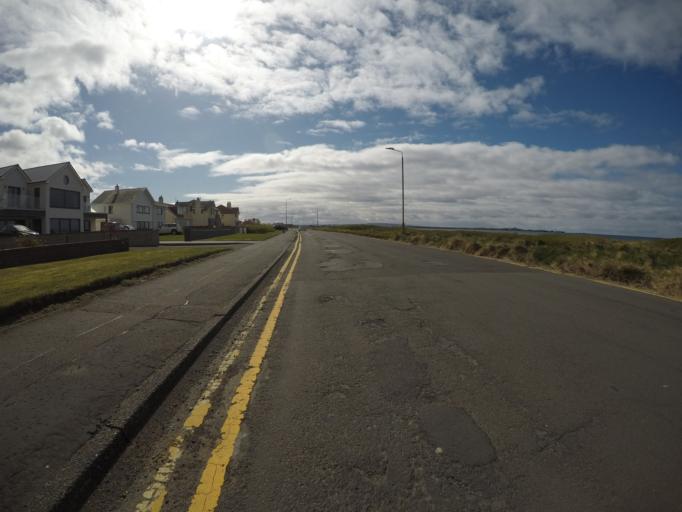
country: GB
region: Scotland
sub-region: South Ayrshire
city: Troon
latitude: 55.5657
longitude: -4.6582
